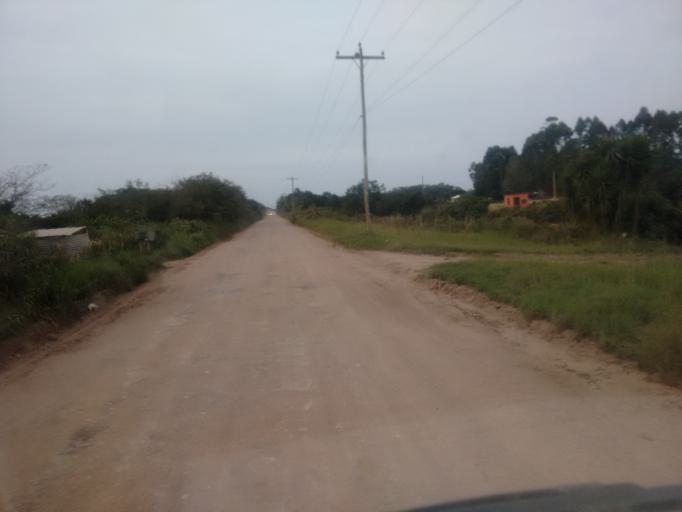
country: BR
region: Rio Grande do Sul
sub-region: Camaqua
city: Camaqua
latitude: -30.9008
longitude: -51.7988
